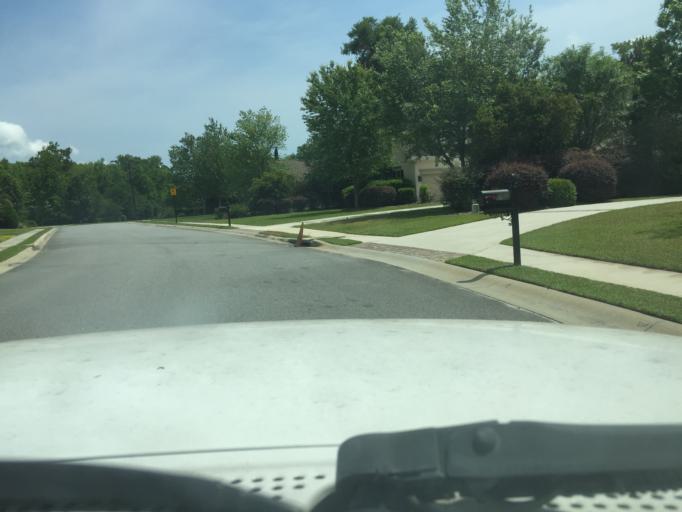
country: US
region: Georgia
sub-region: Chatham County
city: Pooler
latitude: 32.0630
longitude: -81.2443
